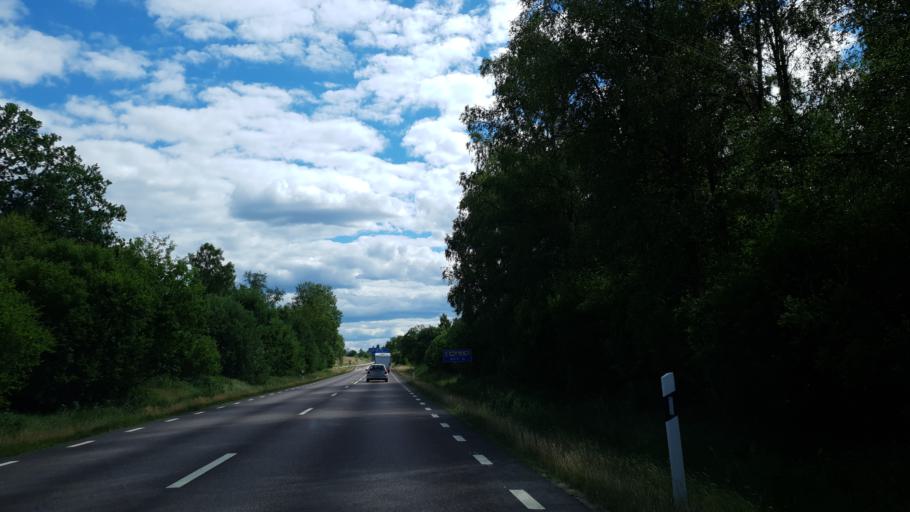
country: SE
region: Kronoberg
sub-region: Lessebo Kommun
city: Lessebo
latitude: 56.8529
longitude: 15.3885
